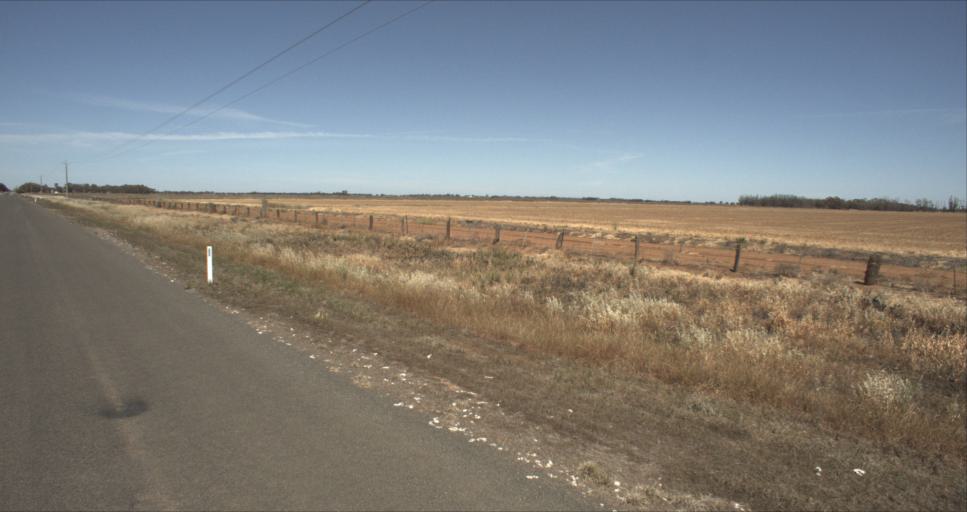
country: AU
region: New South Wales
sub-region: Leeton
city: Leeton
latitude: -34.4853
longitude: 146.2897
